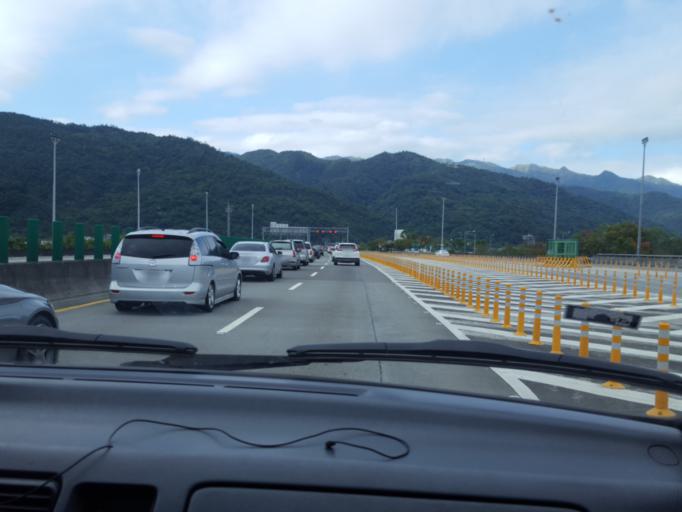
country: TW
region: Taiwan
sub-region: Yilan
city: Yilan
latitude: 24.8337
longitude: 121.7908
